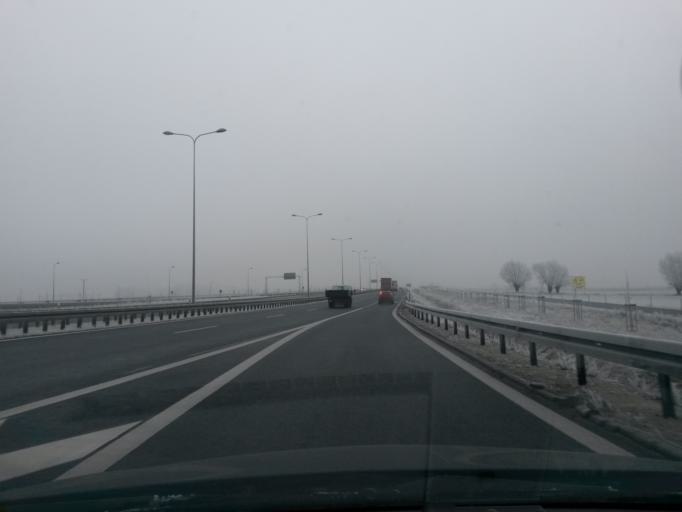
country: PL
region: Greater Poland Voivodeship
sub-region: Powiat gnieznienski
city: Lubowo
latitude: 52.5221
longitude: 17.5103
